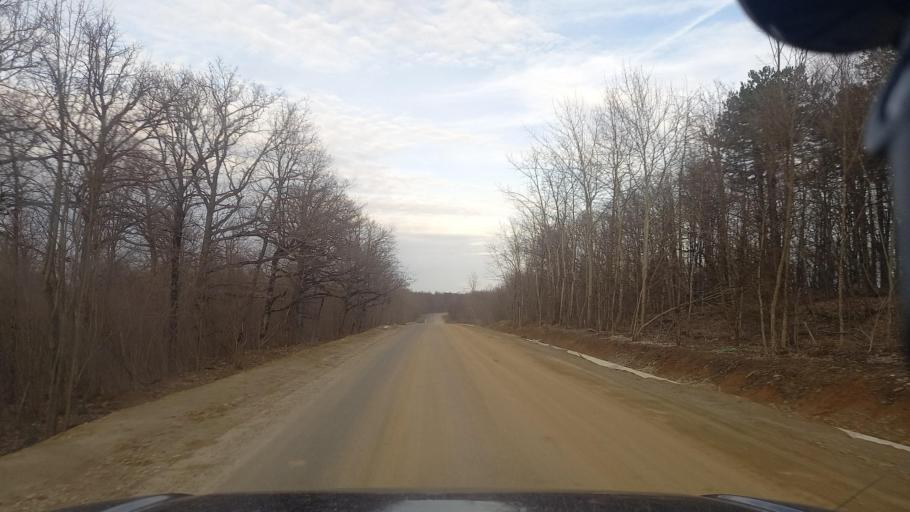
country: RU
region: Krasnodarskiy
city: Goryachiy Klyuch
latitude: 44.7003
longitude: 38.9938
